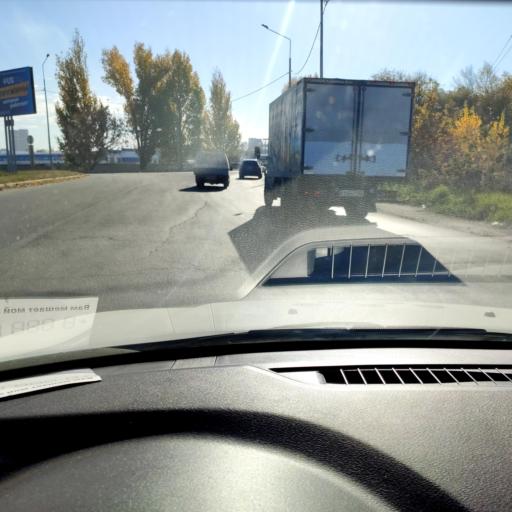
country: RU
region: Samara
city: Tol'yatti
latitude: 53.5725
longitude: 49.4597
